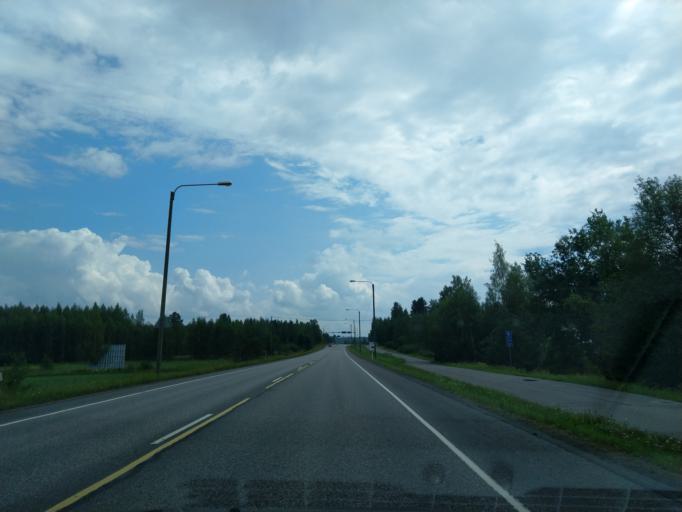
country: FI
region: South Karelia
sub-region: Imatra
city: Parikkala
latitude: 61.5898
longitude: 29.4900
